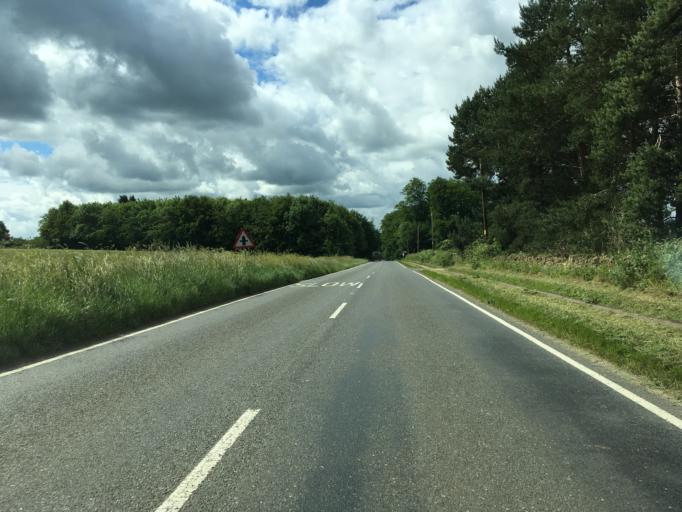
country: GB
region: England
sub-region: Oxfordshire
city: Chipping Norton
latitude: 51.9234
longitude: -1.5415
